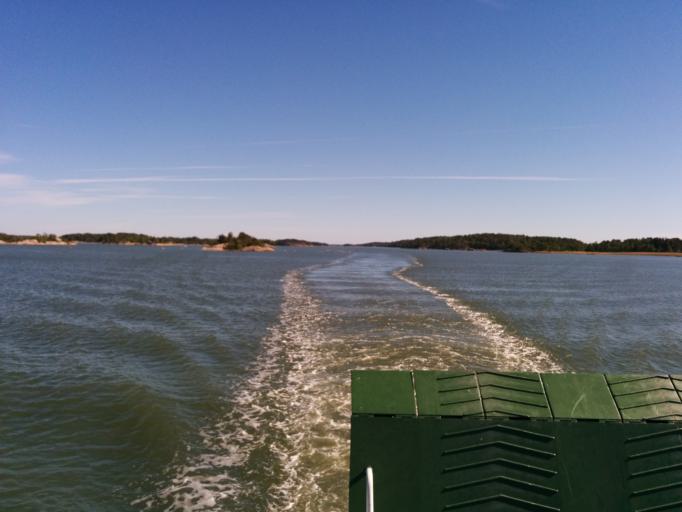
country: FI
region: Varsinais-Suomi
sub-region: Turku
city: Velkua
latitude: 60.4604
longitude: 21.6989
